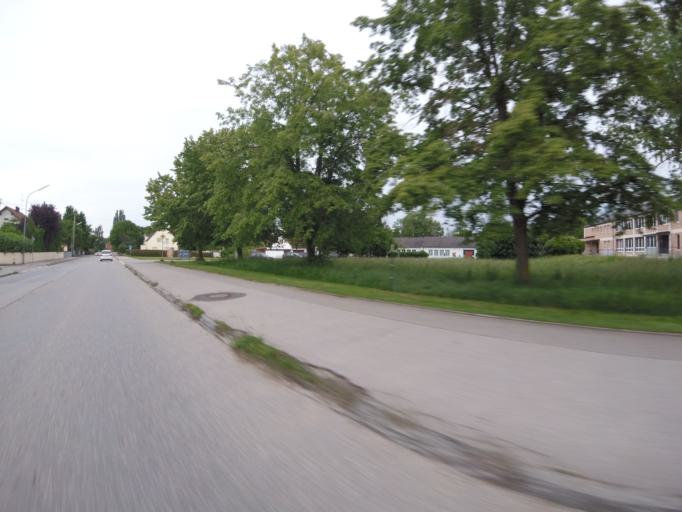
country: DE
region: Bavaria
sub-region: Upper Bavaria
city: Fahrenzhausen
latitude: 48.3534
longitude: 11.5564
